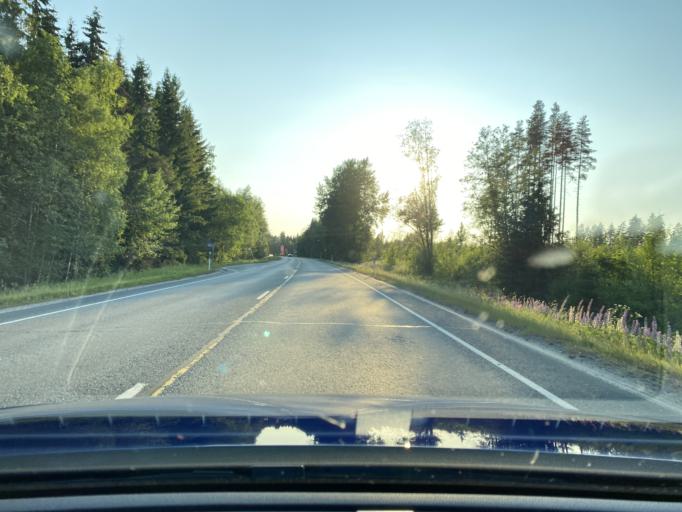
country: FI
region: Haeme
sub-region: Forssa
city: Tammela
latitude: 60.8287
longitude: 23.7323
